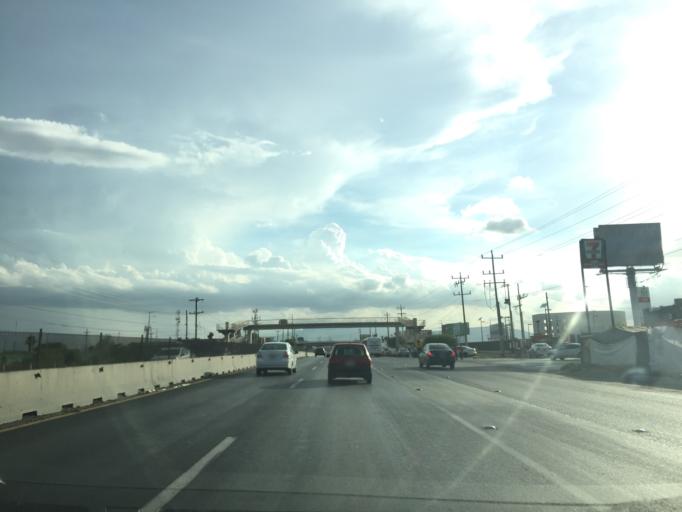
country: MX
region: Nuevo Leon
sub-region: Pesqueria
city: Ladrillera (Entronque Pesqueria)
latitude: 25.7914
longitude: -100.1383
